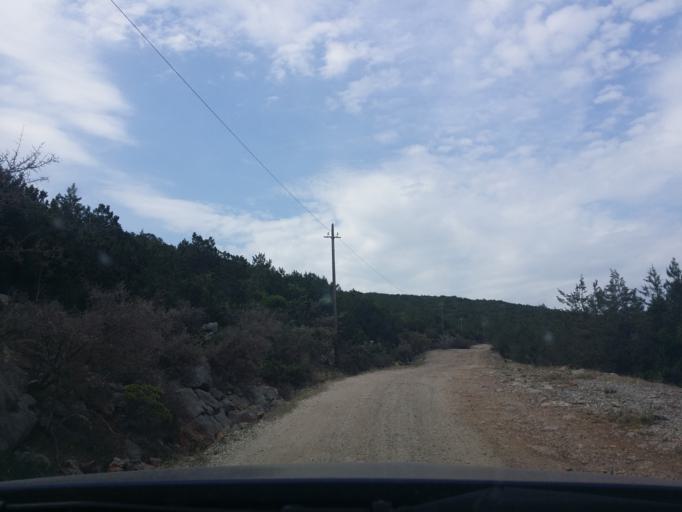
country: GR
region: Attica
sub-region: Nomos Piraios
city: Poros
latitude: 37.5324
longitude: 23.4753
